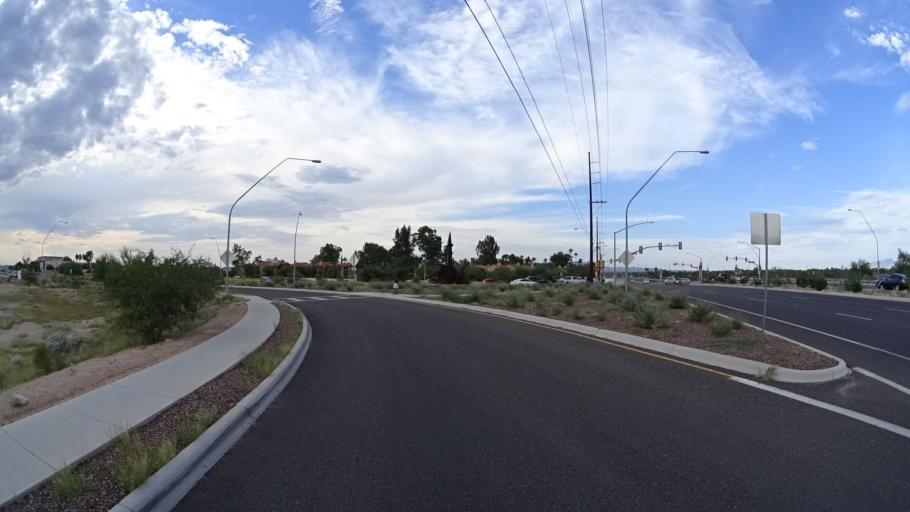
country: US
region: Arizona
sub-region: Pima County
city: Casas Adobes
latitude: 32.3469
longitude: -111.0131
